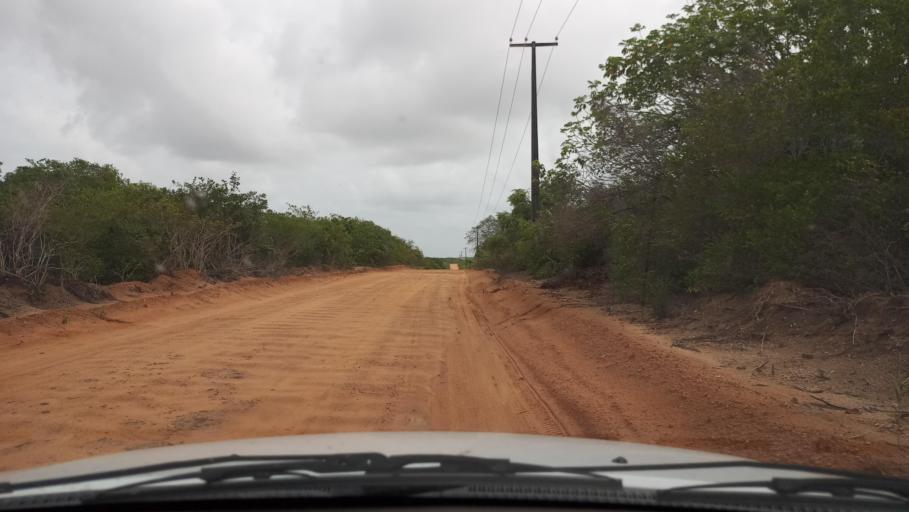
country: BR
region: Rio Grande do Norte
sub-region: Maxaranguape
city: Sao Miguel
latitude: -5.4794
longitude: -35.3028
